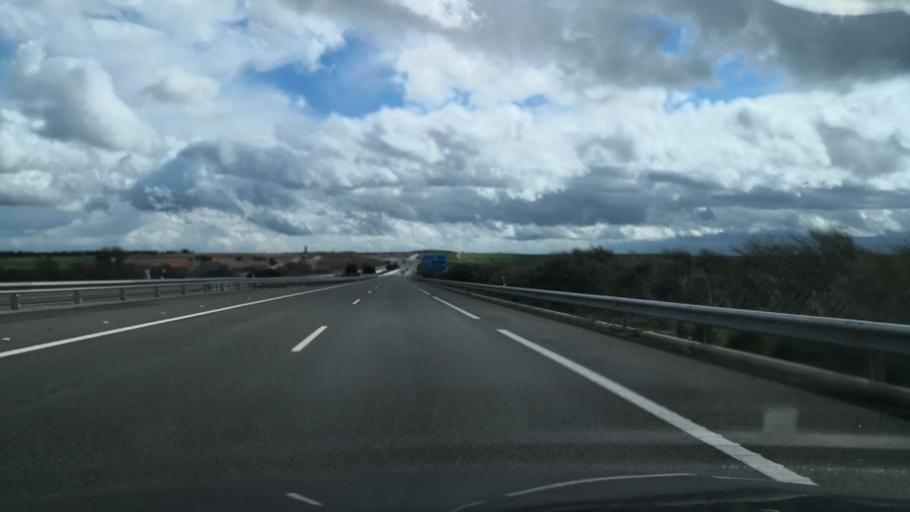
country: ES
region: Castille and Leon
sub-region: Provincia de Salamanca
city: Calzada de Valdunciel
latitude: 41.1353
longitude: -5.6974
